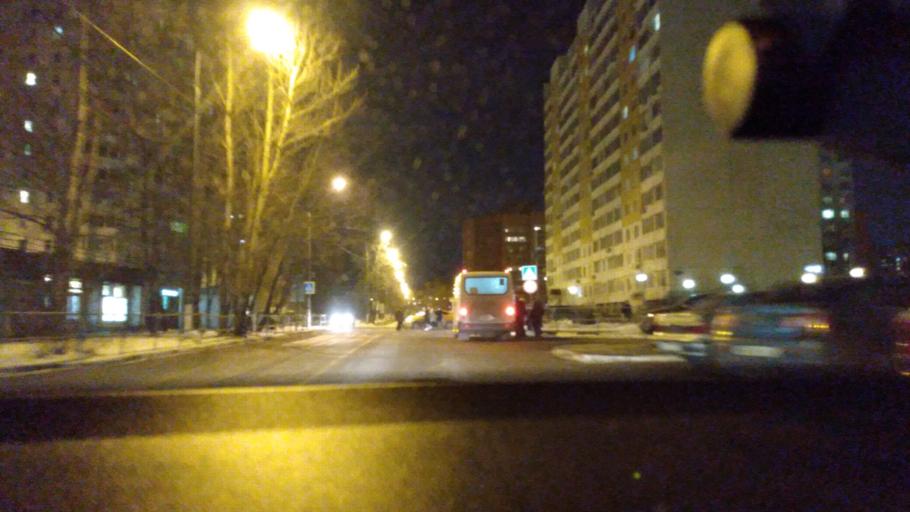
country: RU
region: Moskovskaya
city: Zheleznodorozhnyy
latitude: 55.7464
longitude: 38.0225
